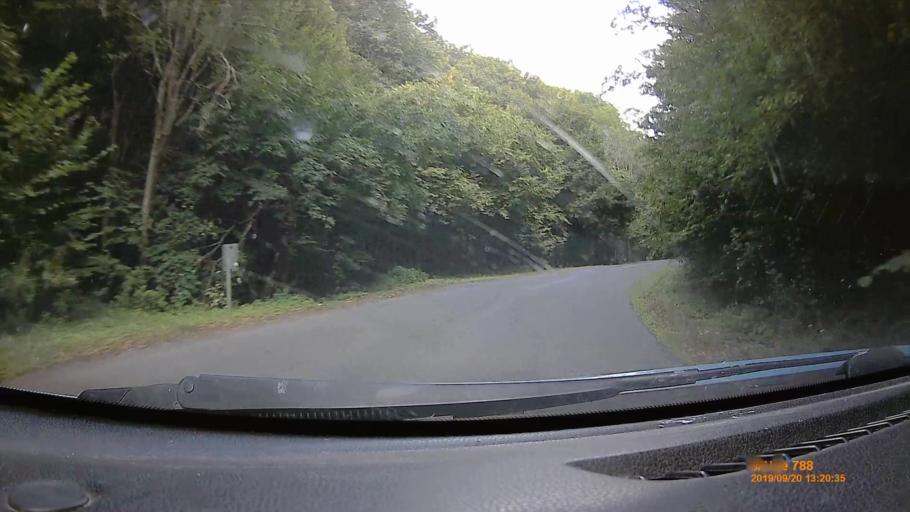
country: HU
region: Heves
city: Felsotarkany
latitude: 48.0148
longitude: 20.4648
